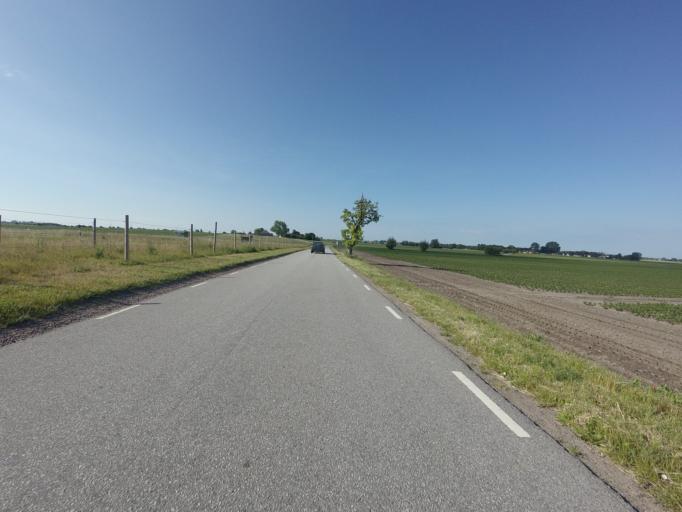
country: SE
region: Skane
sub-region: Trelleborgs Kommun
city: Skare
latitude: 55.4196
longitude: 13.0189
